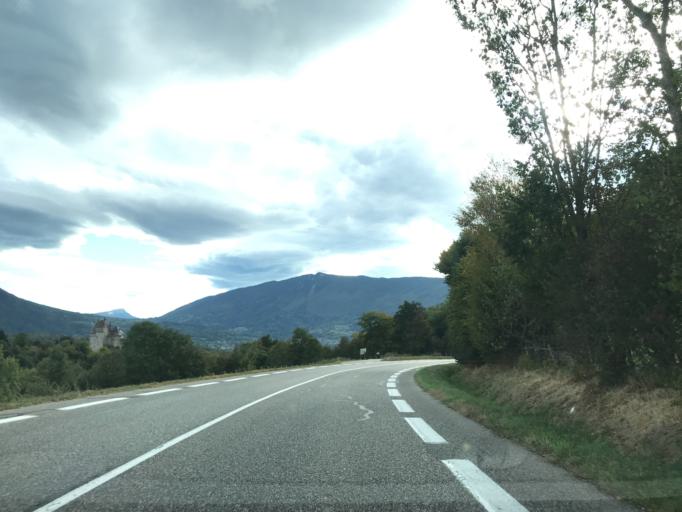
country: FR
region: Rhone-Alpes
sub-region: Departement de la Haute-Savoie
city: Menthon-Saint-Bernard
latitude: 45.8693
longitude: 6.2074
